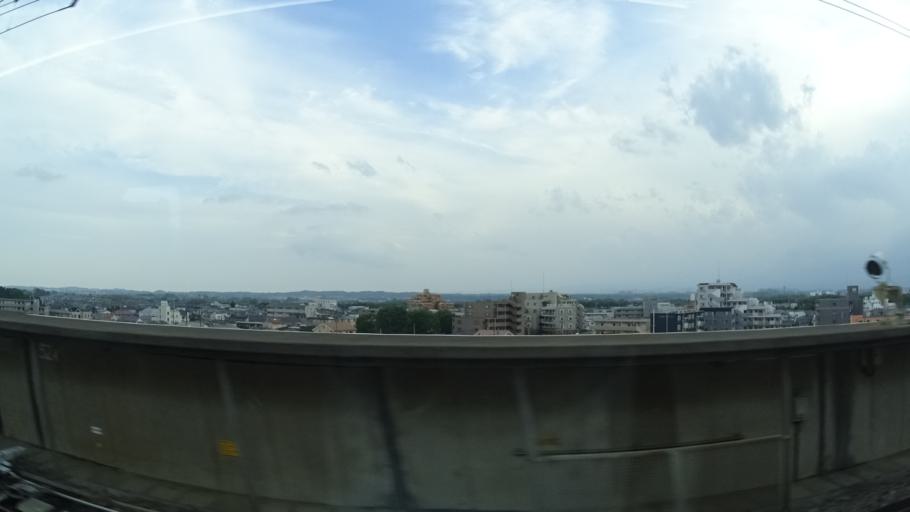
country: JP
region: Saitama
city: Kumagaya
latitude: 36.1379
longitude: 139.3938
